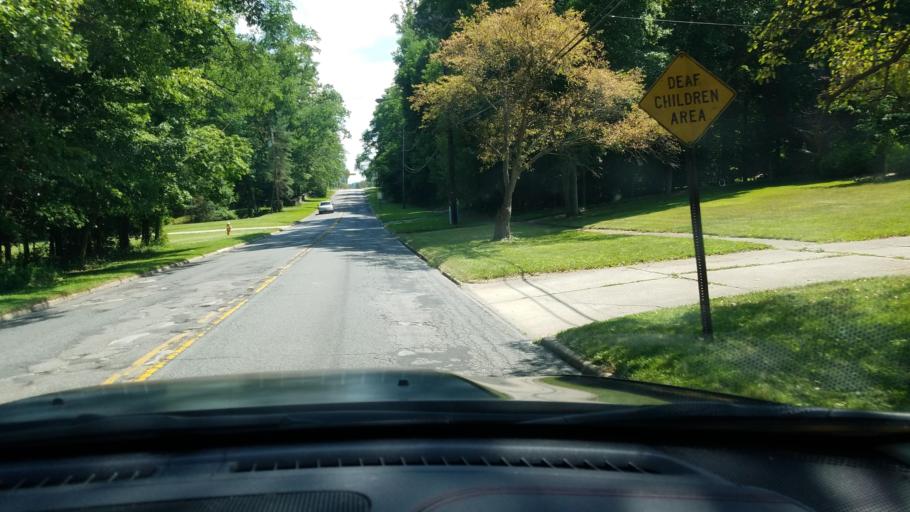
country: US
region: Ohio
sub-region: Mahoning County
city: Youngstown
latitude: 41.0794
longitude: -80.6998
